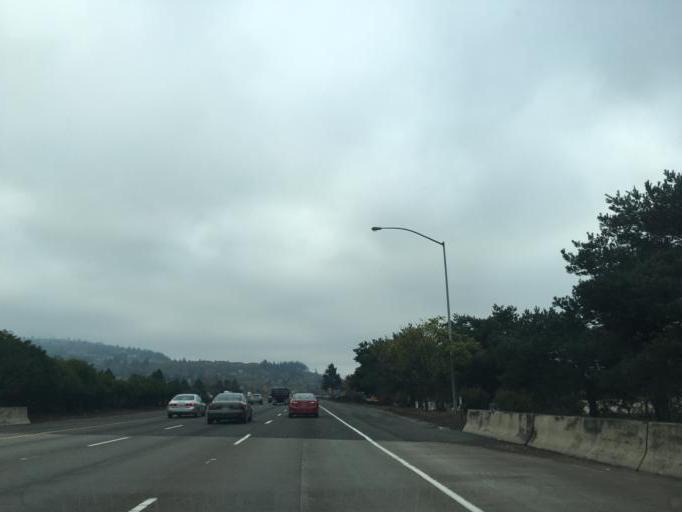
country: US
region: Oregon
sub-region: Multnomah County
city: Lents
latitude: 45.4783
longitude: -122.5660
